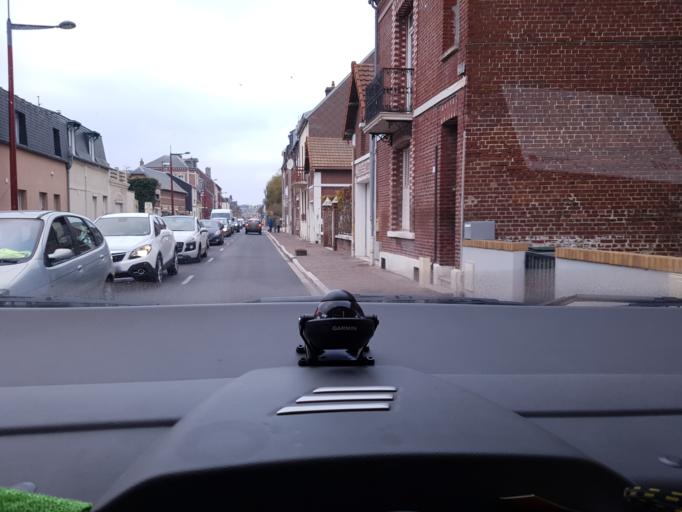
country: FR
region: Picardie
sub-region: Departement de la Somme
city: Mers-les-Bains
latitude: 50.0651
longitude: 1.3929
